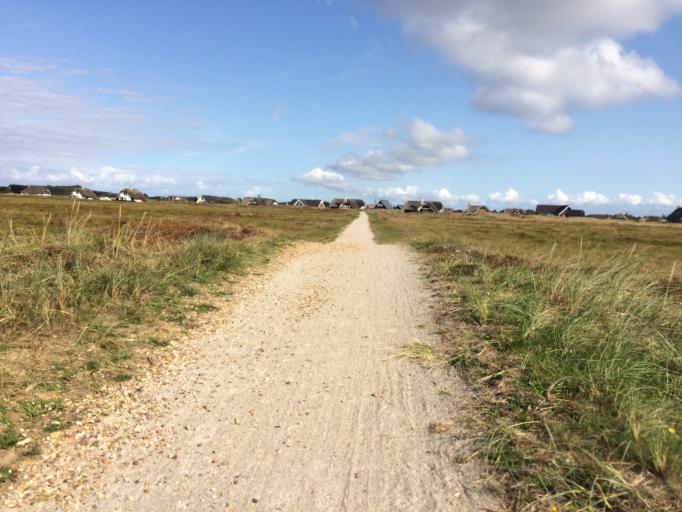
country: DK
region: Central Jutland
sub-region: Ringkobing-Skjern Kommune
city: Hvide Sande
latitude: 55.8837
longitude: 8.1688
